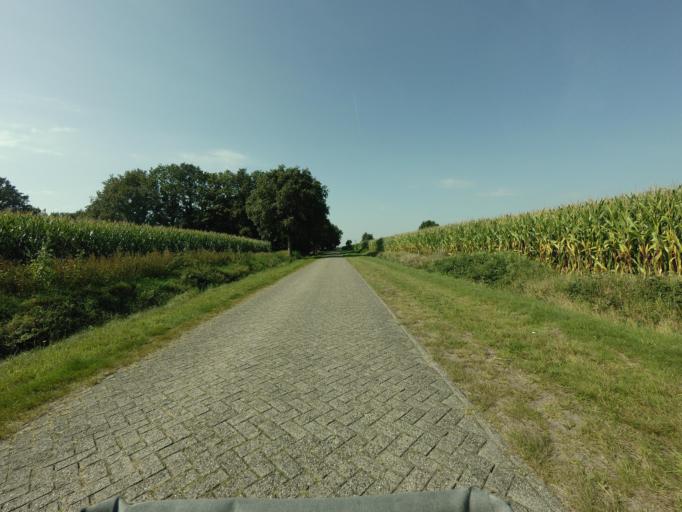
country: DE
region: Lower Saxony
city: Emlichheim
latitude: 52.5776
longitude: 6.8200
